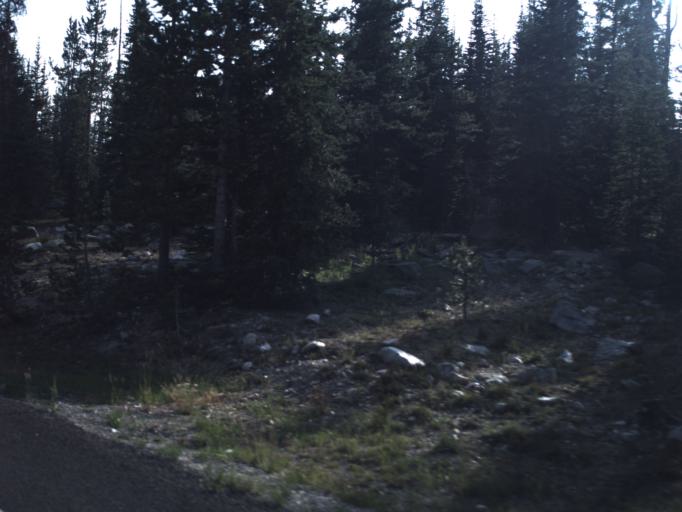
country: US
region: Utah
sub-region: Summit County
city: Kamas
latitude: 40.7182
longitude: -110.8776
